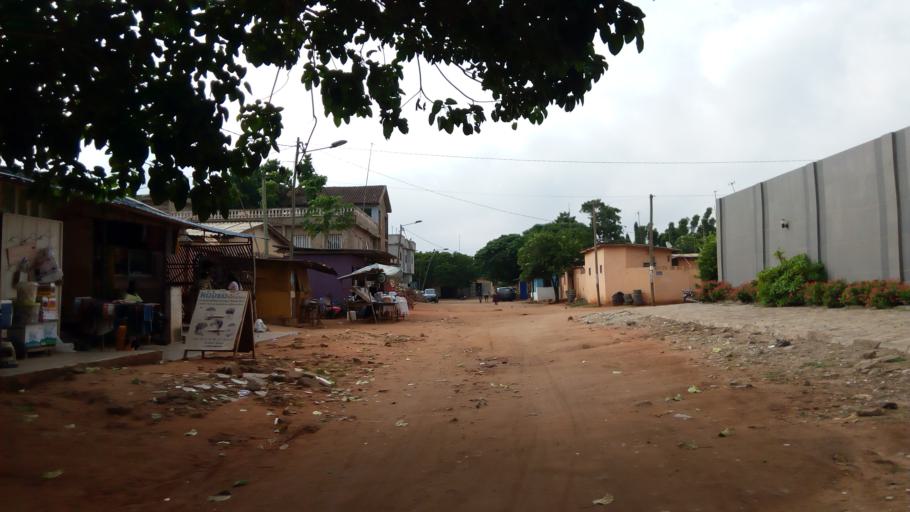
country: TG
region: Maritime
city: Lome
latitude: 6.1833
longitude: 1.1923
